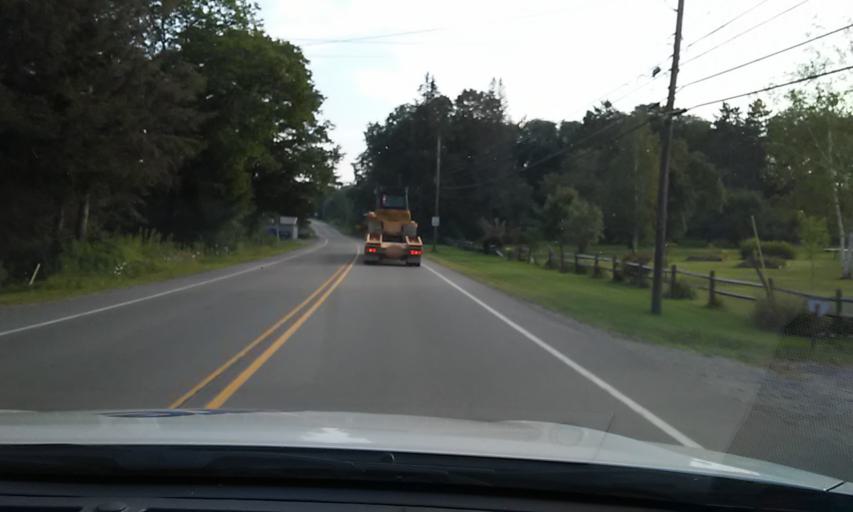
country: US
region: Pennsylvania
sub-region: McKean County
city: Kane
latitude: 41.7144
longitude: -78.6908
